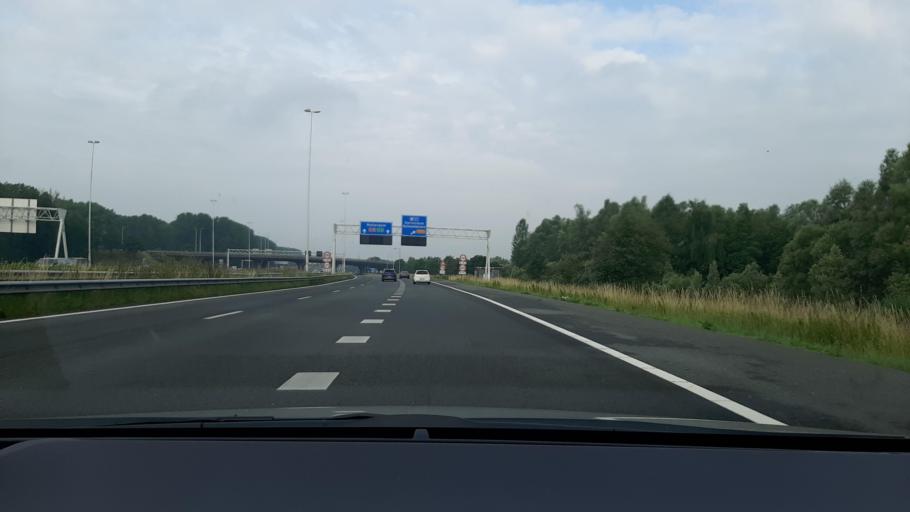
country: NL
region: South Holland
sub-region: Gemeente Gorinchem
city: Gorinchem
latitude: 51.8454
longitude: 4.9447
